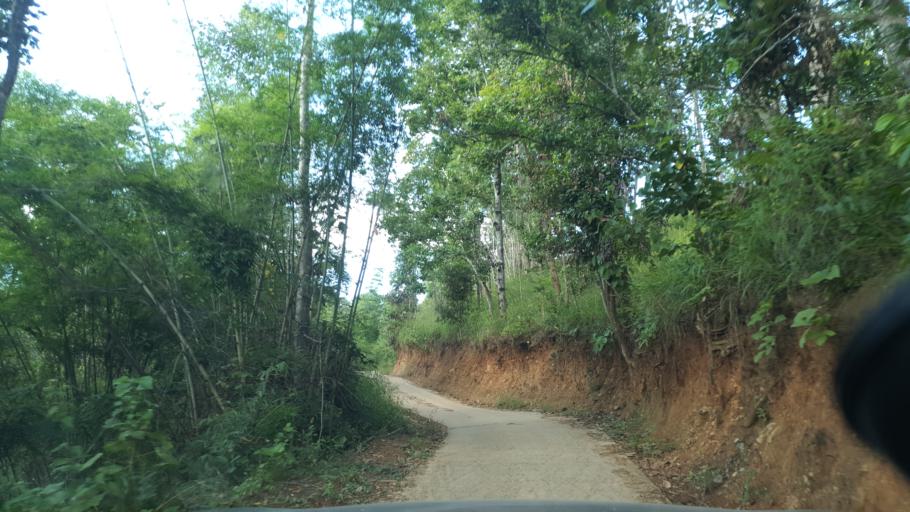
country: TH
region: Chiang Mai
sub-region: Amphoe Chiang Dao
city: Chiang Dao
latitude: 19.4083
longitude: 98.8327
